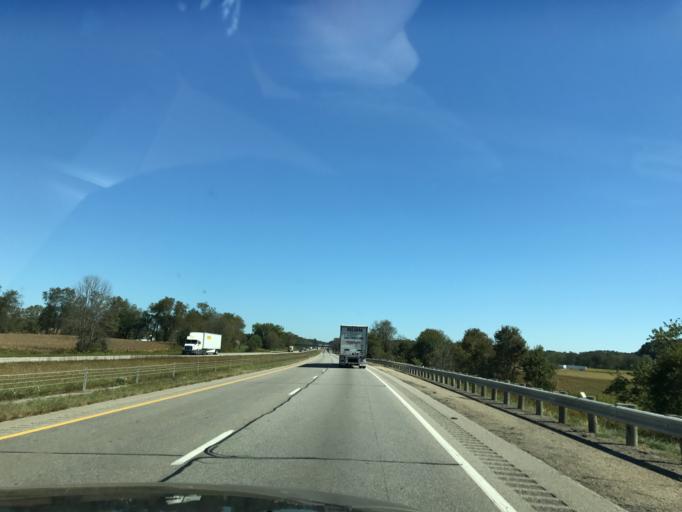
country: US
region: Ohio
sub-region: Perry County
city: Somerset
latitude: 39.9371
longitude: -82.2446
